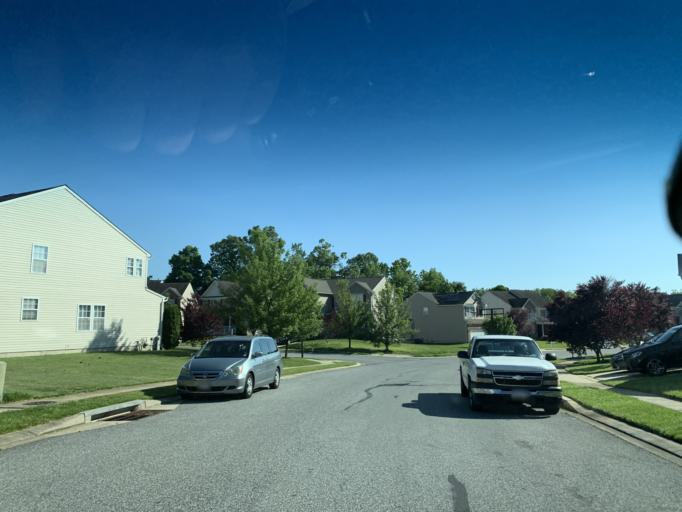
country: US
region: Maryland
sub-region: Harford County
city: Riverside
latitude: 39.4813
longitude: -76.2373
